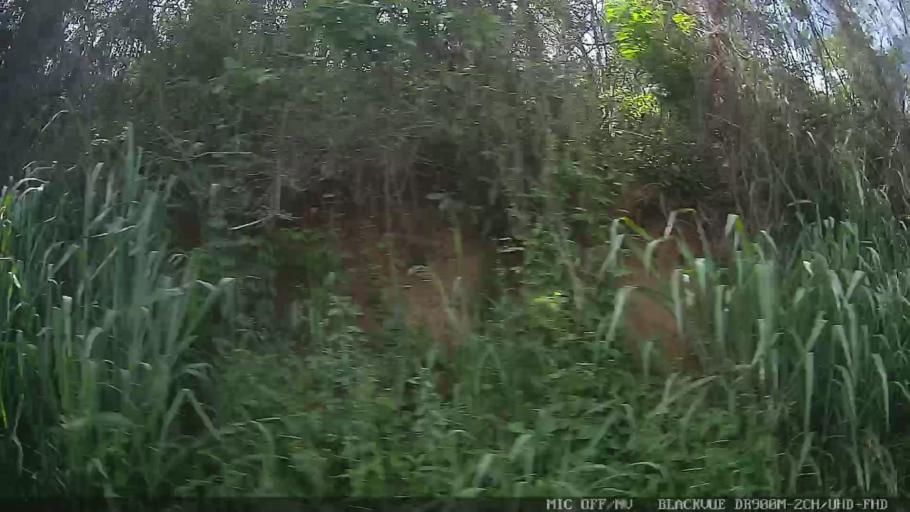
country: BR
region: Sao Paulo
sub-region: Braganca Paulista
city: Braganca Paulista
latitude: -22.9598
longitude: -46.6262
